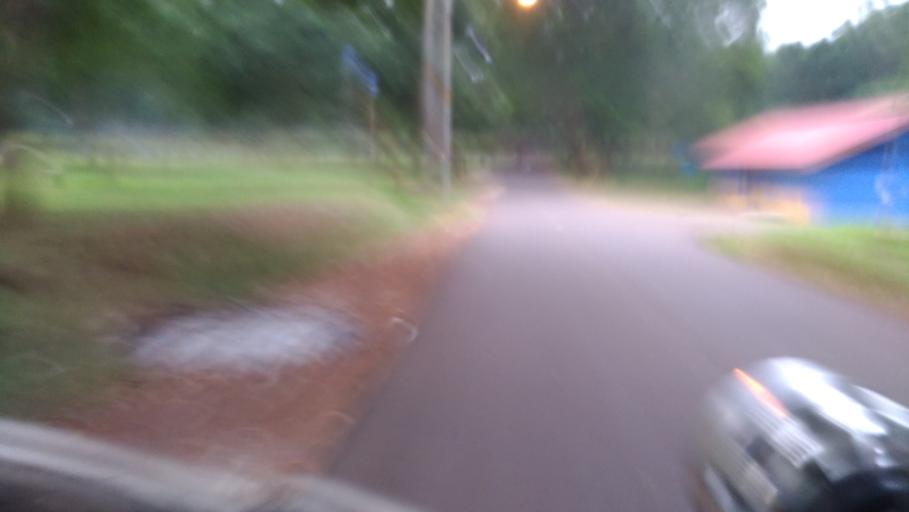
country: ID
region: West Java
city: Cileungsir
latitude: -6.3621
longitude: 106.8982
